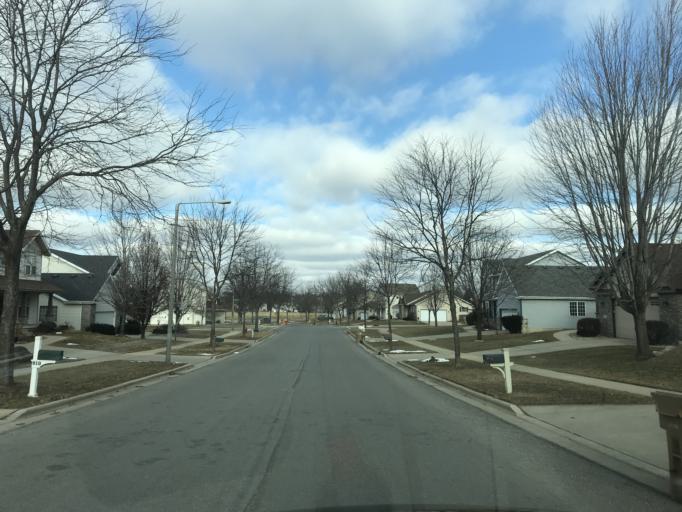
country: US
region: Wisconsin
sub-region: Dane County
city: Monona
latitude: 43.1108
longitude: -89.2912
